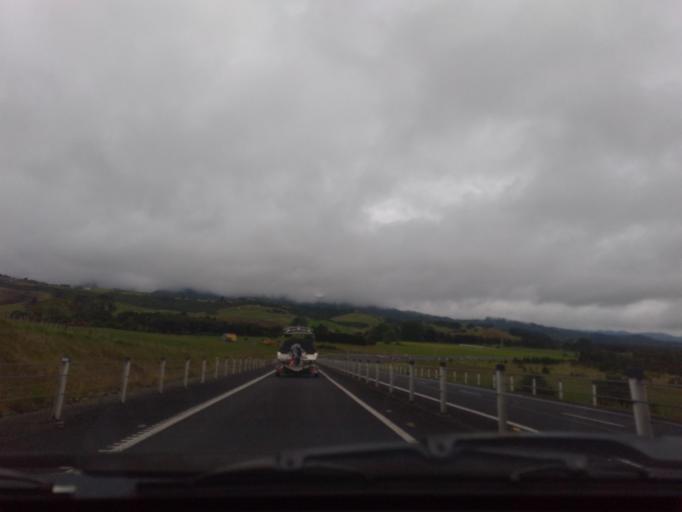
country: NZ
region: Northland
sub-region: Whangarei
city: Ruakaka
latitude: -36.0365
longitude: 174.4170
